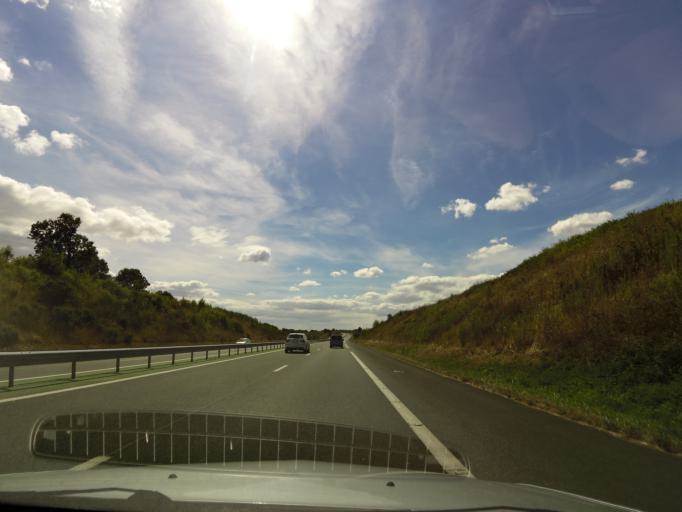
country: FR
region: Pays de la Loire
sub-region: Departement de la Vendee
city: Les Essarts
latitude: 46.7956
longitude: -1.2308
